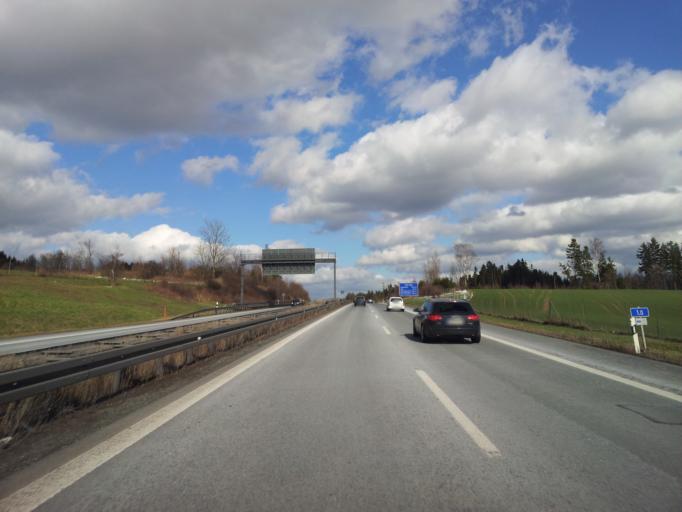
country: DE
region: Bavaria
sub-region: Upper Franconia
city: Leupoldsgrun
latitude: 50.3309
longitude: 11.8050
